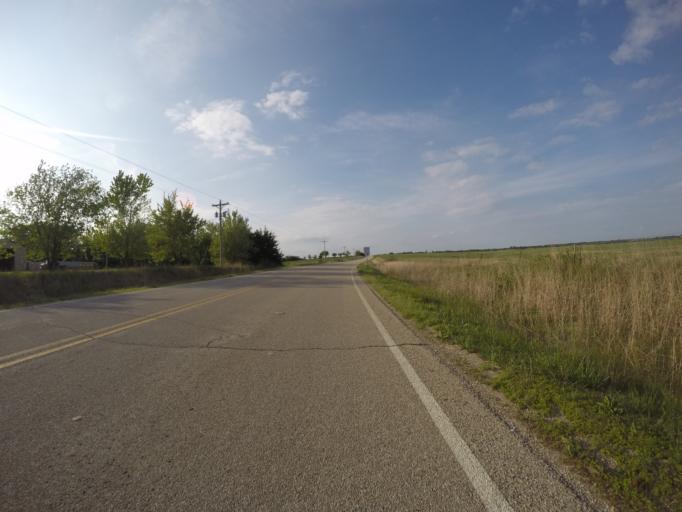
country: US
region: Kansas
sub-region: Pottawatomie County
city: Westmoreland
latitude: 39.4070
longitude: -96.6071
